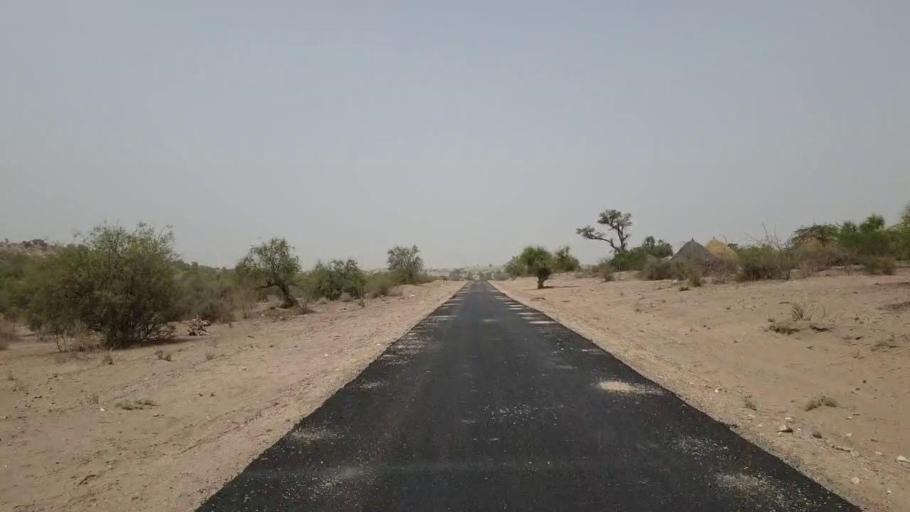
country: PK
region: Sindh
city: Islamkot
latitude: 24.8106
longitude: 70.5663
